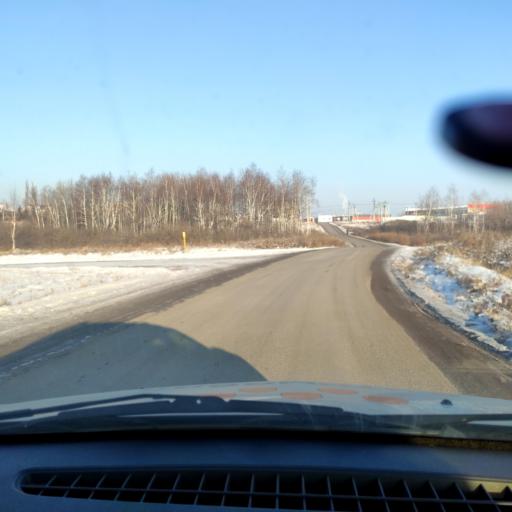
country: RU
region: Bashkortostan
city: Ufa
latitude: 54.6128
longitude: 55.9204
